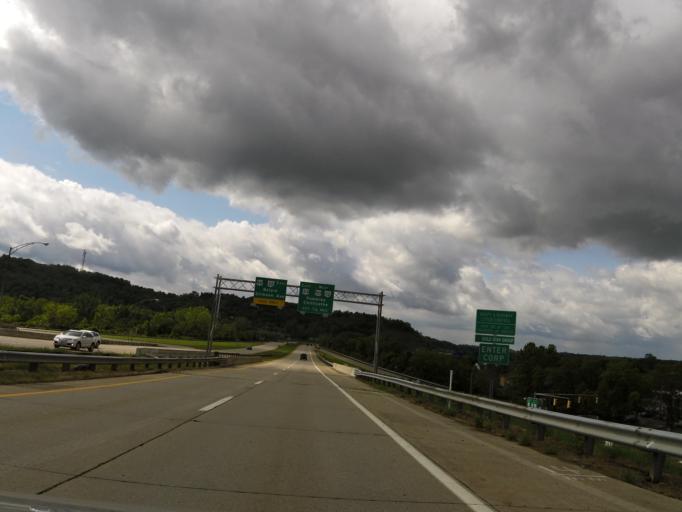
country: US
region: Ohio
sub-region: Athens County
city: Athens
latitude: 39.3382
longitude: -82.0816
